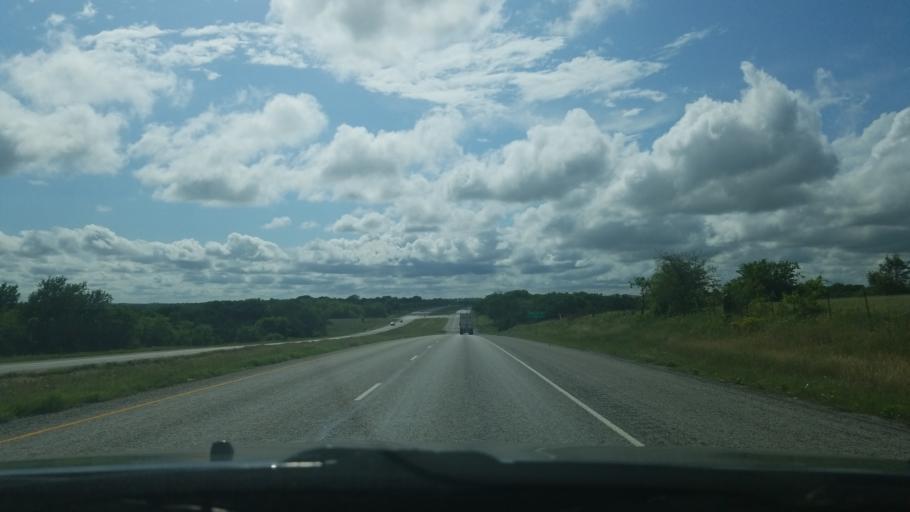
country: US
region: Texas
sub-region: Denton County
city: Ponder
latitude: 33.2452
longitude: -97.3847
